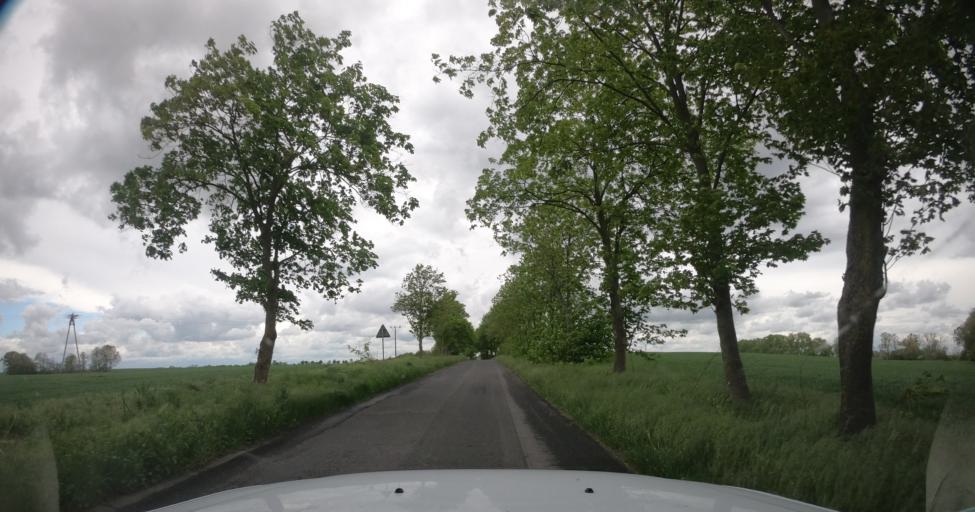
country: PL
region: West Pomeranian Voivodeship
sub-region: Powiat pyrzycki
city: Kozielice
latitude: 53.1188
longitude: 14.8086
